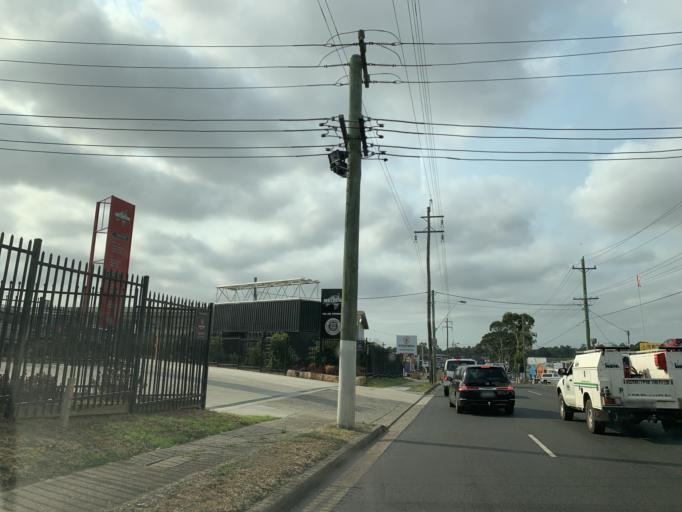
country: AU
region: New South Wales
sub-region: Blacktown
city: Blacktown
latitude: -33.7700
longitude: 150.9434
